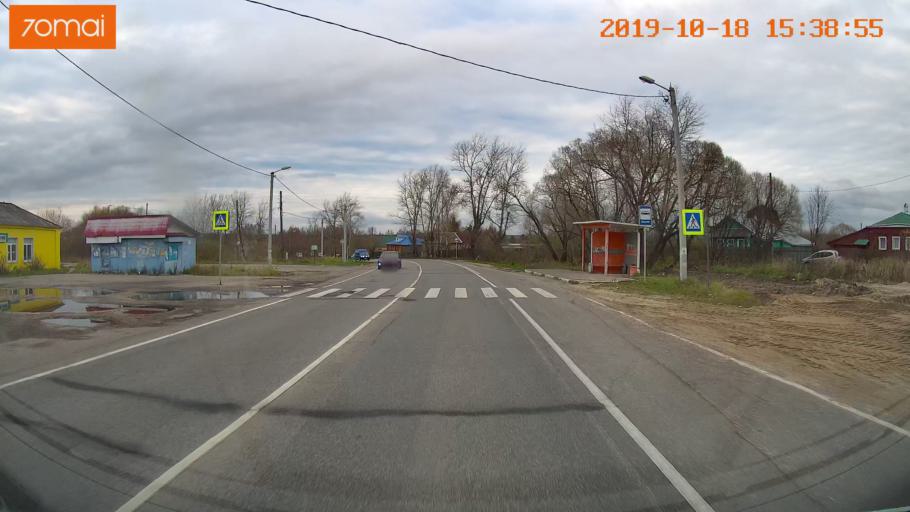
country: RU
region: Vladimir
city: Golovino
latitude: 55.9169
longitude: 40.6075
